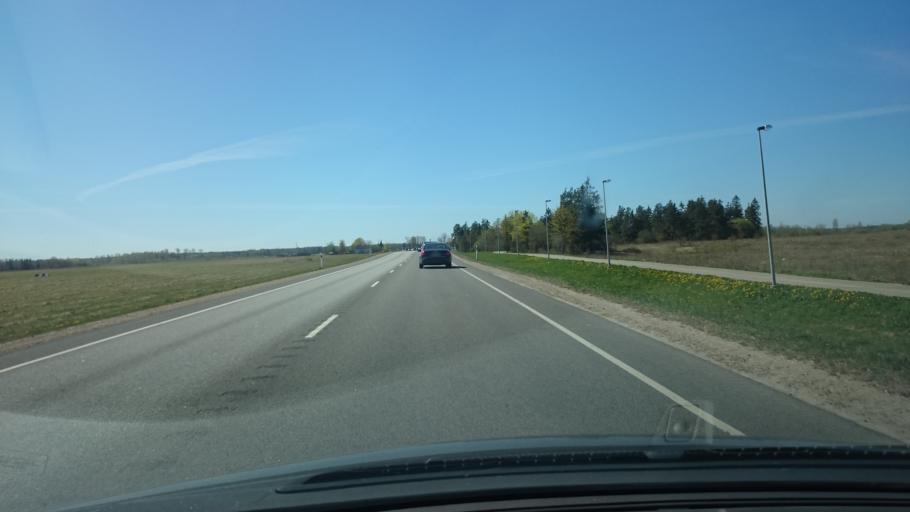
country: EE
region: Ida-Virumaa
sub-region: Narva linn
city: Narva
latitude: 59.3892
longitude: 28.1217
